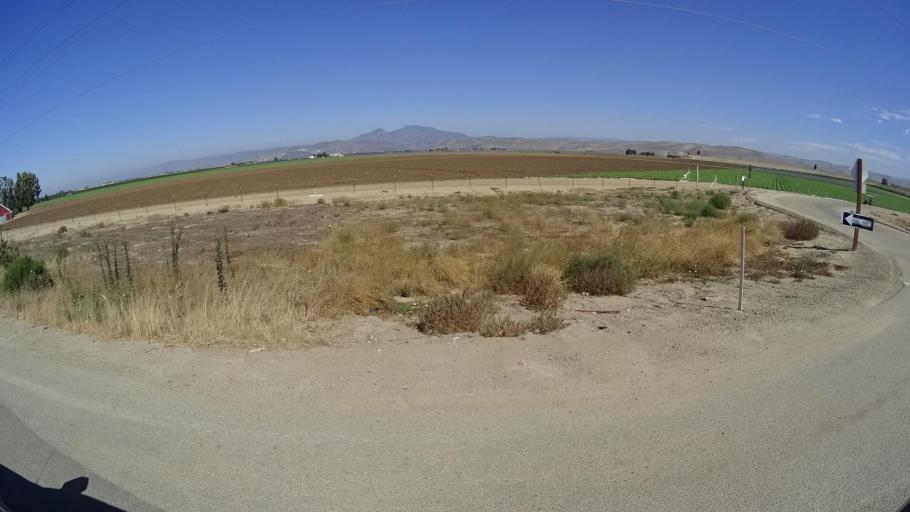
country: US
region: California
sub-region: Monterey County
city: Greenfield
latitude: 36.2965
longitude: -121.2189
